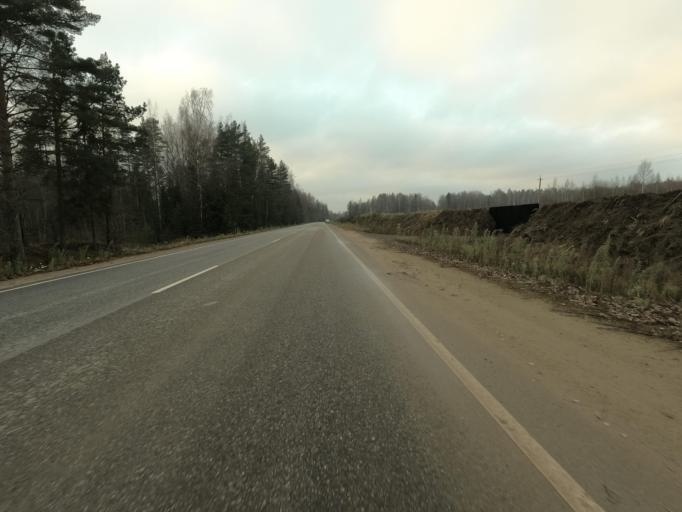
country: RU
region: Leningrad
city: Kirovsk
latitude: 59.8025
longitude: 30.9806
